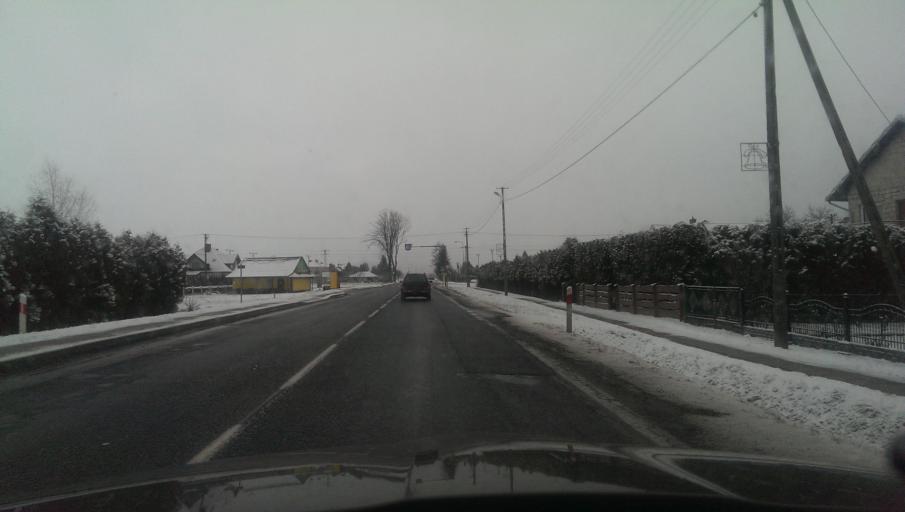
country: PL
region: Subcarpathian Voivodeship
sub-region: Powiat sanocki
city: Besko
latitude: 49.5853
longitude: 21.9647
